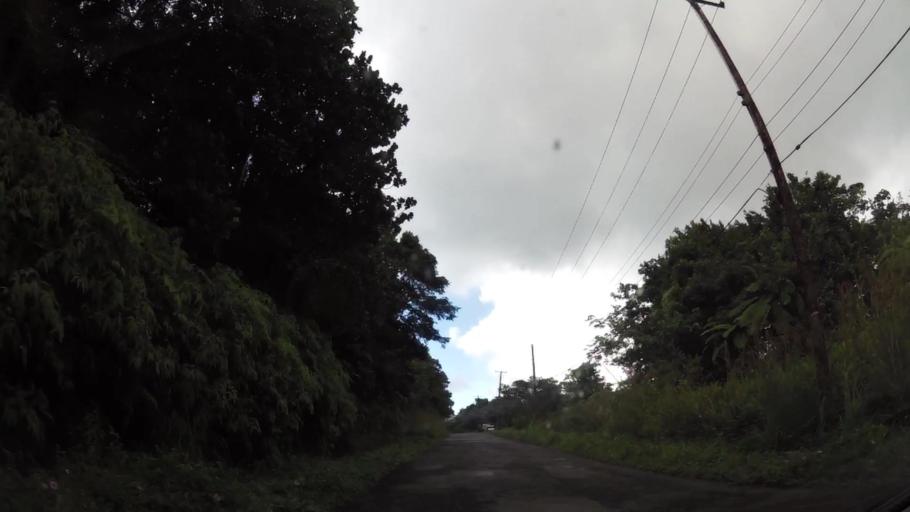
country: DM
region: Saint Paul
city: Pont Casse
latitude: 15.3911
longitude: -61.3148
